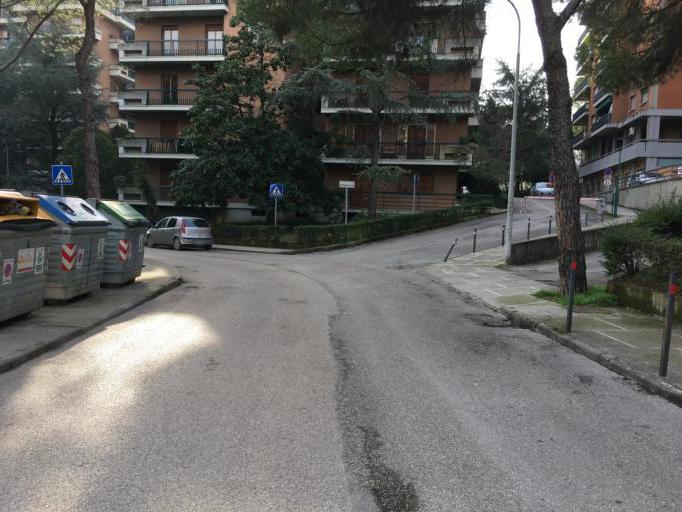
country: IT
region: Umbria
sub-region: Provincia di Perugia
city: Perugia
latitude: 43.1000
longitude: 12.3672
